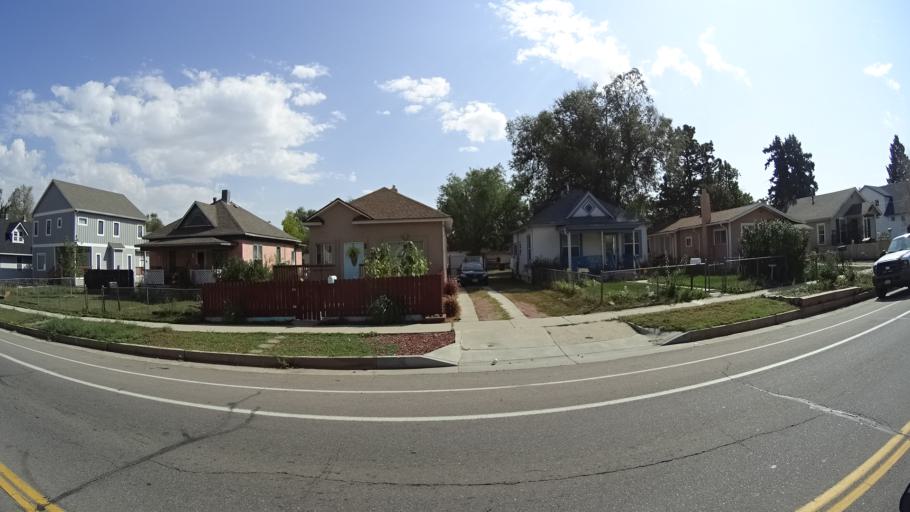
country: US
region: Colorado
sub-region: El Paso County
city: Colorado Springs
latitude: 38.8253
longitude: -104.8043
